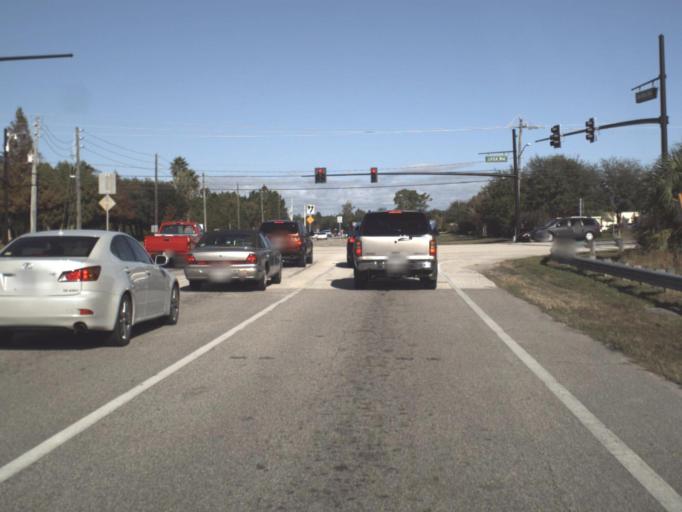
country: US
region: Florida
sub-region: Volusia County
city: Holly Hill
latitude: 29.2265
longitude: -81.0864
